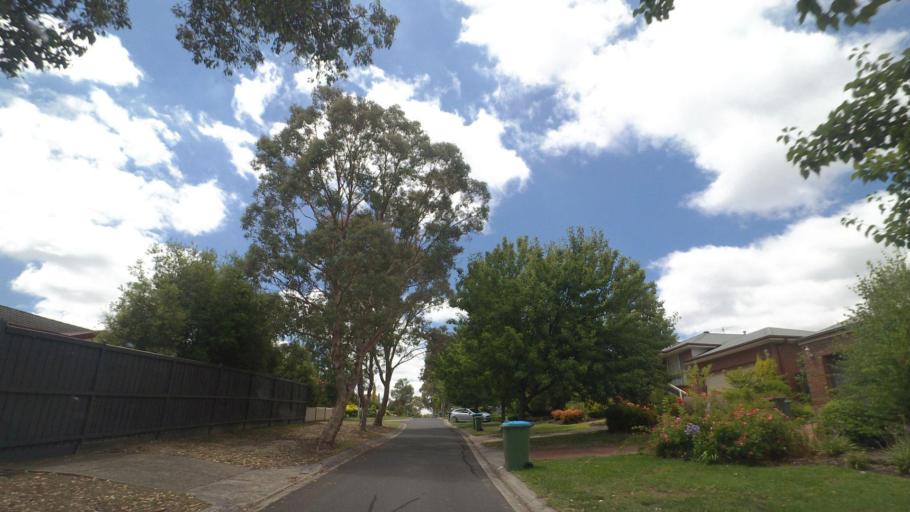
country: AU
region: Victoria
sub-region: Maroondah
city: Croydon Hills
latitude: -37.7674
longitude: 145.2674
